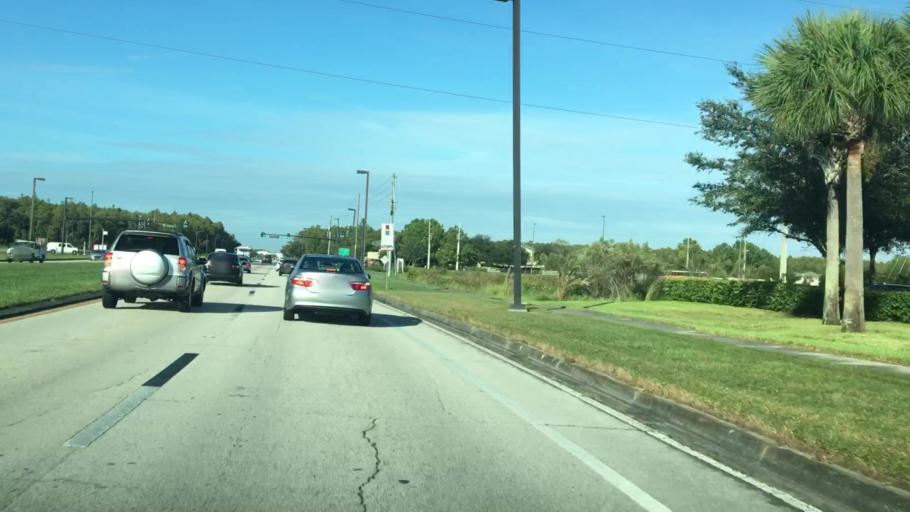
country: US
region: Florida
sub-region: Orange County
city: Conway
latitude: 28.4662
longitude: -81.2880
